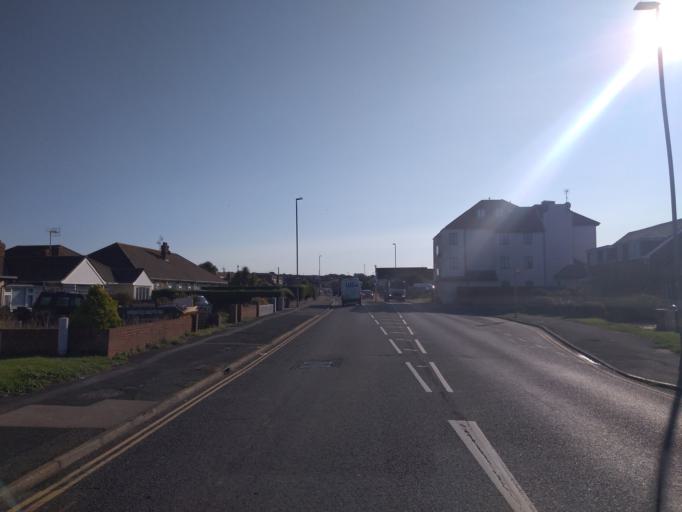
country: GB
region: England
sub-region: East Sussex
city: Peacehaven
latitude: 50.7887
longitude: 0.0130
